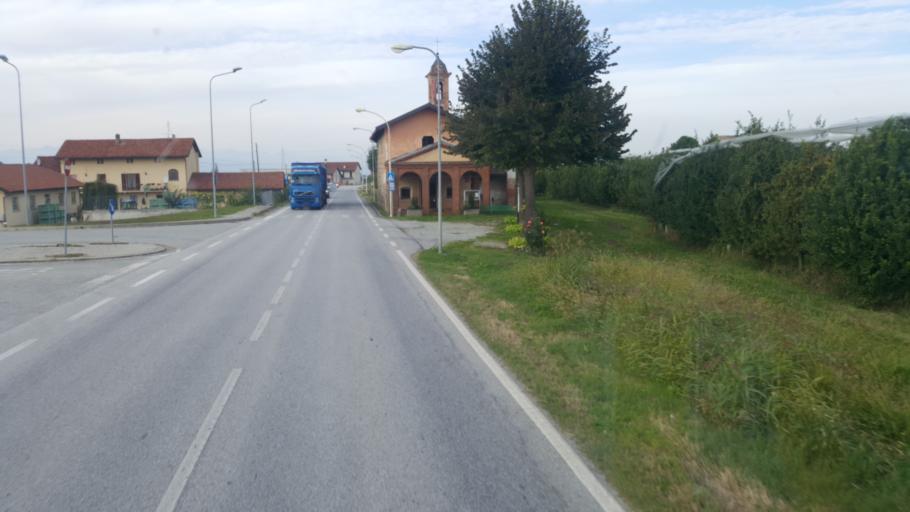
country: IT
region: Piedmont
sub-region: Provincia di Cuneo
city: Manta
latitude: 44.6189
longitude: 7.5089
